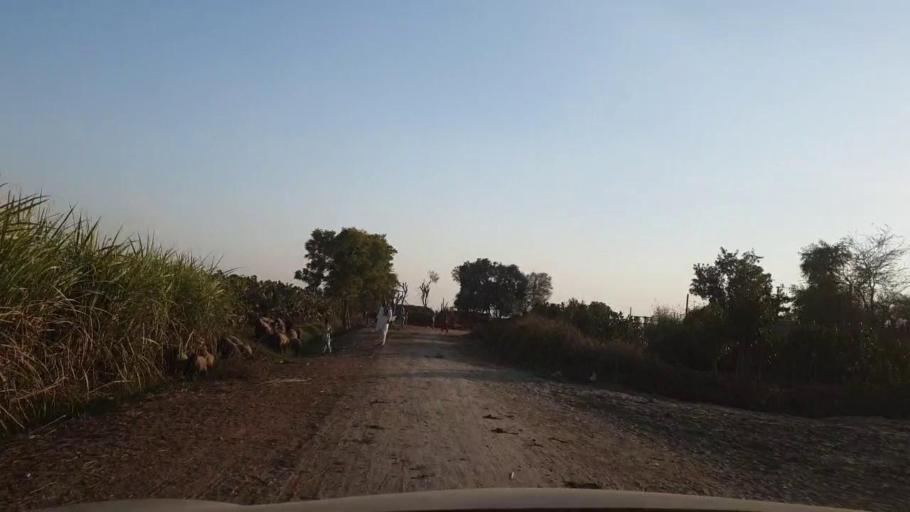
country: PK
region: Sindh
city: Tando Allahyar
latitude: 25.5880
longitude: 68.6982
